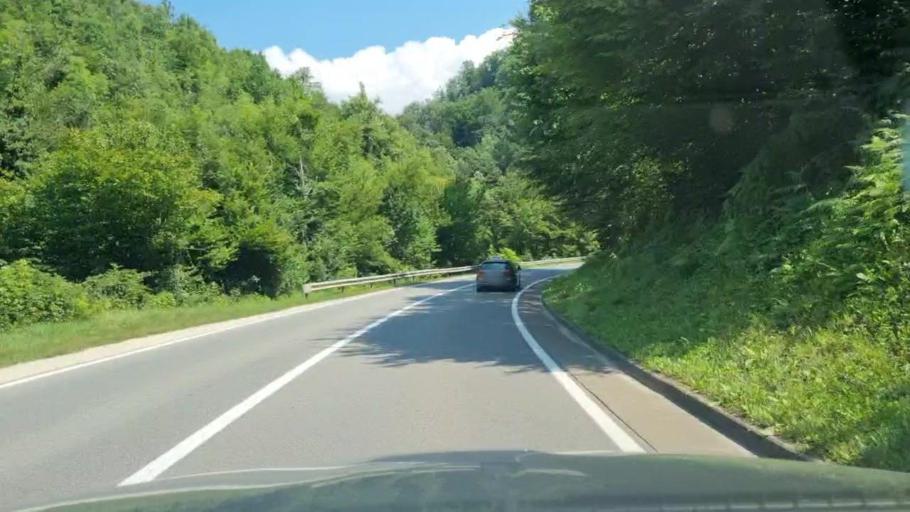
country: BA
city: Stupari
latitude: 44.3575
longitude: 18.6728
